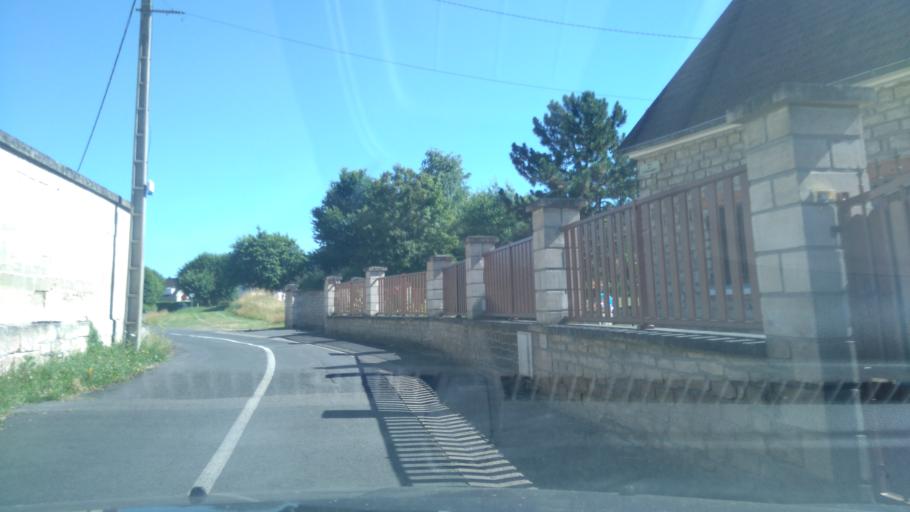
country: FR
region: Picardie
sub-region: Departement de l'Oise
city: Saint-Maximin
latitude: 49.2226
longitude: 2.4499
